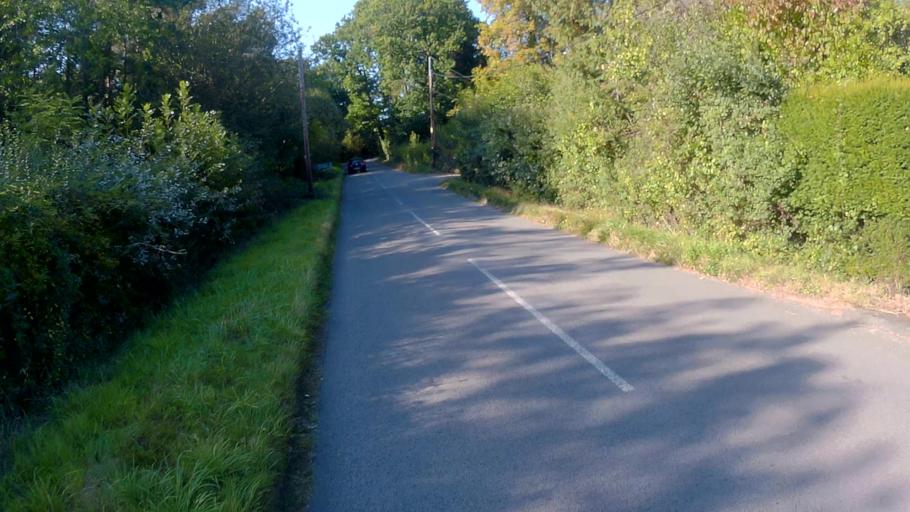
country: GB
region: England
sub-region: Hampshire
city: Lindford
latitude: 51.1594
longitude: -0.8320
